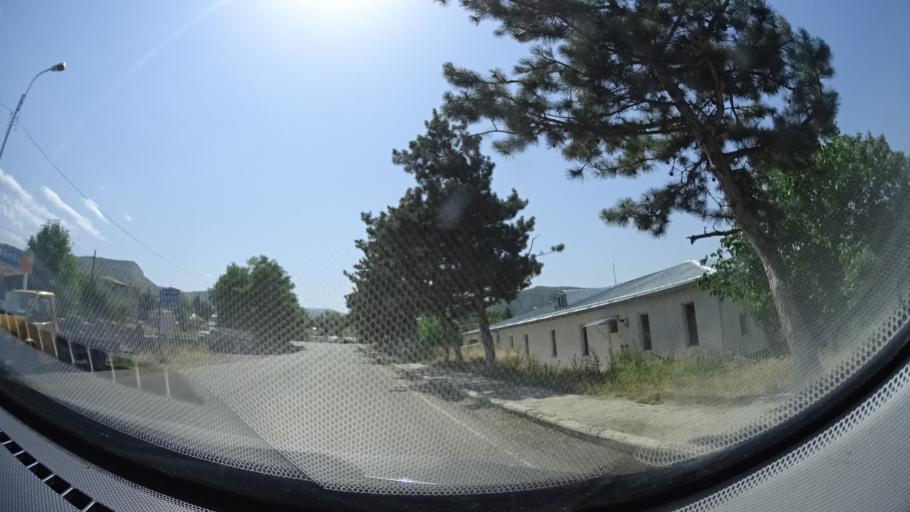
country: GE
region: Samtskhe-Javakheti
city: Aspindza
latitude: 41.5739
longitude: 43.2475
